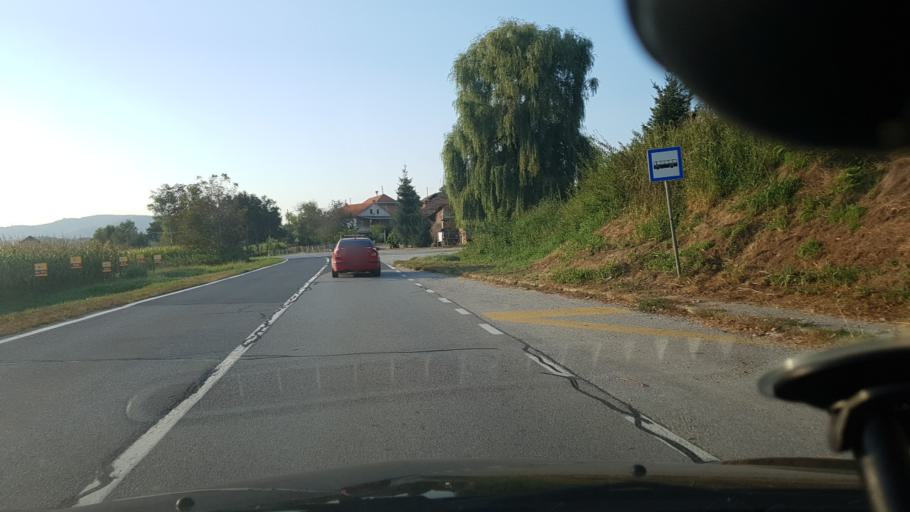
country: HR
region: Krapinsko-Zagorska
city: Pregrada
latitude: 46.1351
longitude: 15.7952
